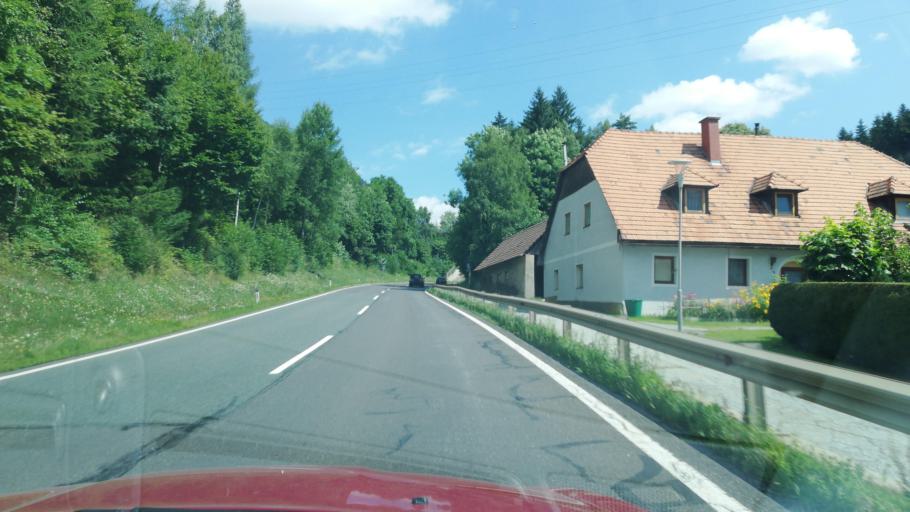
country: AT
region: Styria
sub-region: Politischer Bezirk Murau
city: Durnstein in der Steiermark
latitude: 47.0030
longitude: 14.3964
